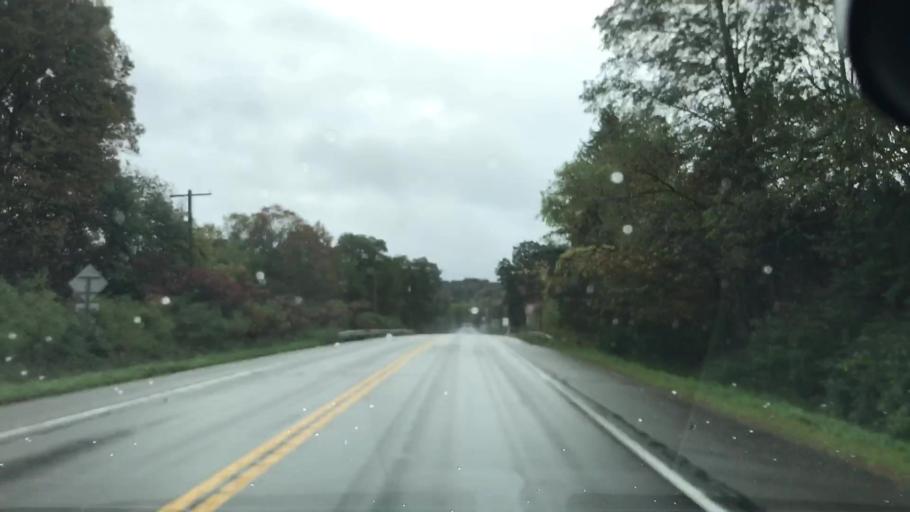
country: US
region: New York
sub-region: Erie County
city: Springville
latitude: 42.4102
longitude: -78.6897
